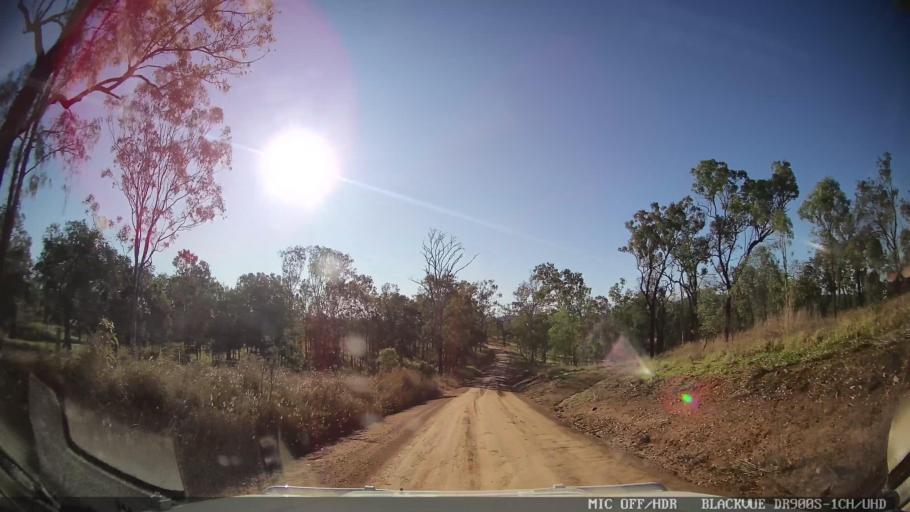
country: AU
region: Queensland
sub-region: Bundaberg
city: Sharon
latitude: -24.7892
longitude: 151.6076
